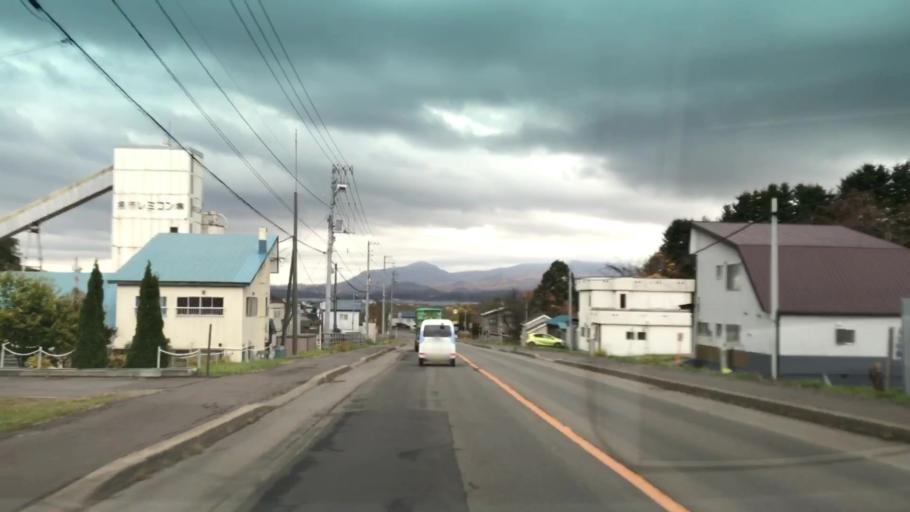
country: JP
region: Hokkaido
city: Yoichi
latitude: 43.2107
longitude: 140.7528
